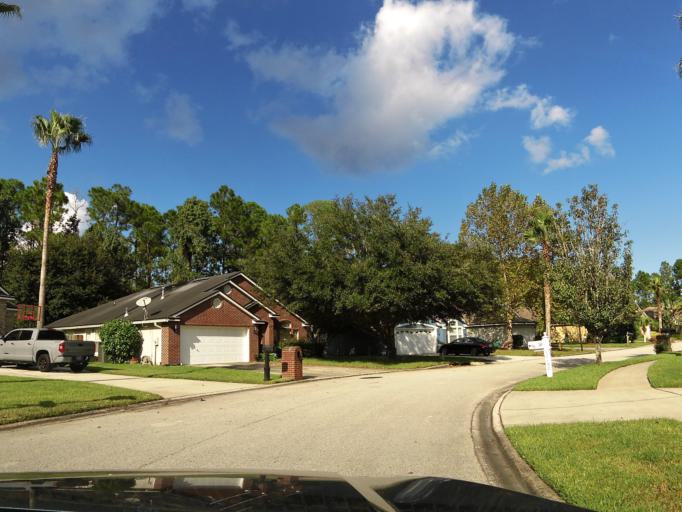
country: US
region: Florida
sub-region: Duval County
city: Jacksonville Beach
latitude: 30.2797
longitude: -81.4994
